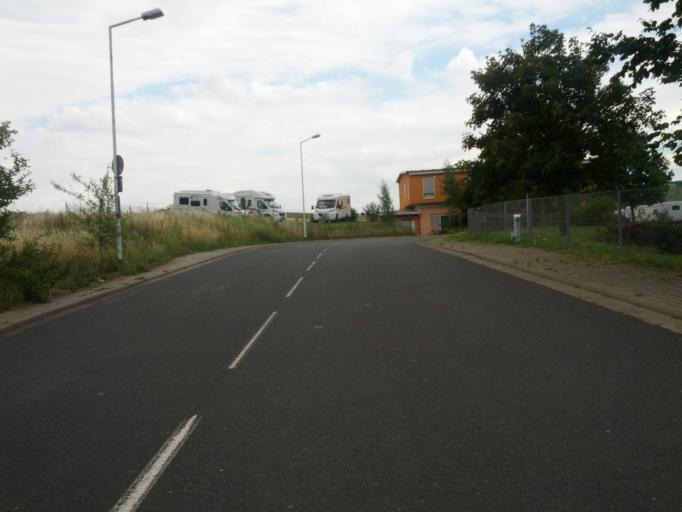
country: DE
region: Thuringia
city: Eisenach
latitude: 51.0028
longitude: 10.3265
